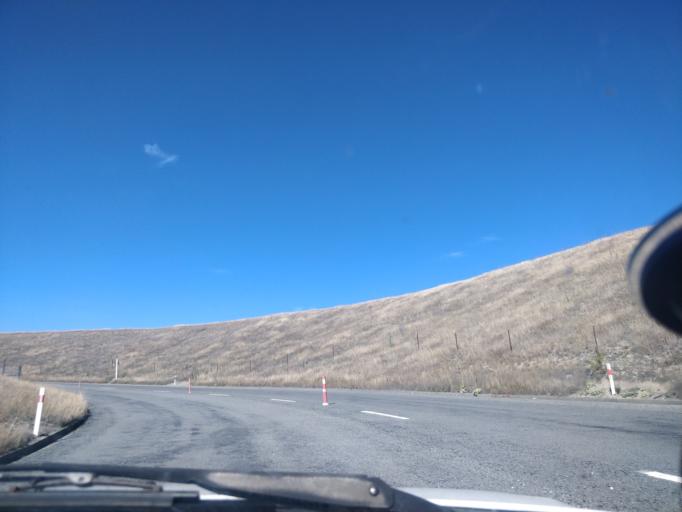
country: NZ
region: Otago
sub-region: Queenstown-Lakes District
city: Wanaka
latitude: -44.2660
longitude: 170.0331
